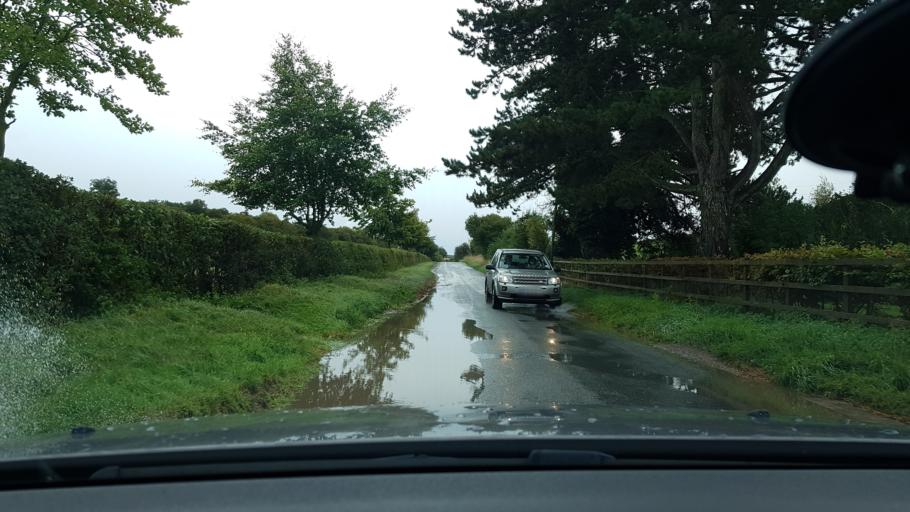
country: GB
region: England
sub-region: West Berkshire
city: Lambourn
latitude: 51.5332
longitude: -1.5271
